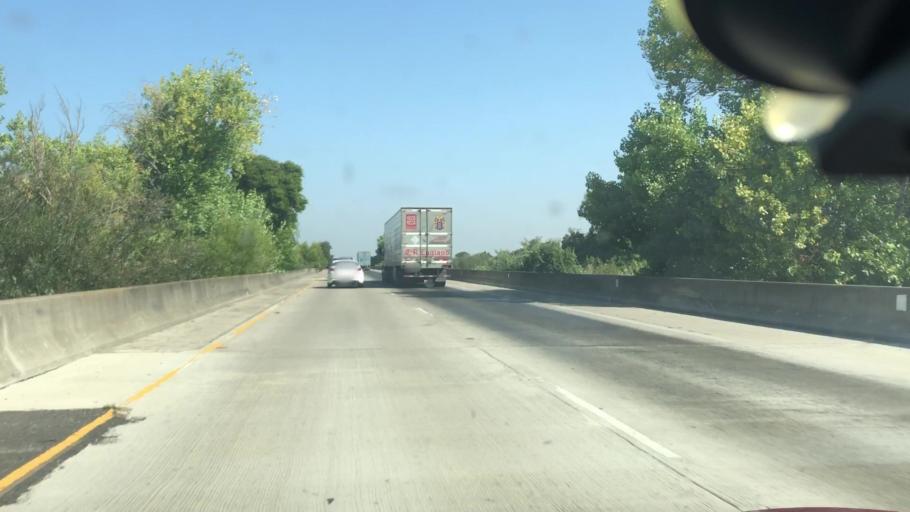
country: US
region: California
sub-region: San Joaquin County
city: Thornton
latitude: 38.2690
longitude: -121.4532
